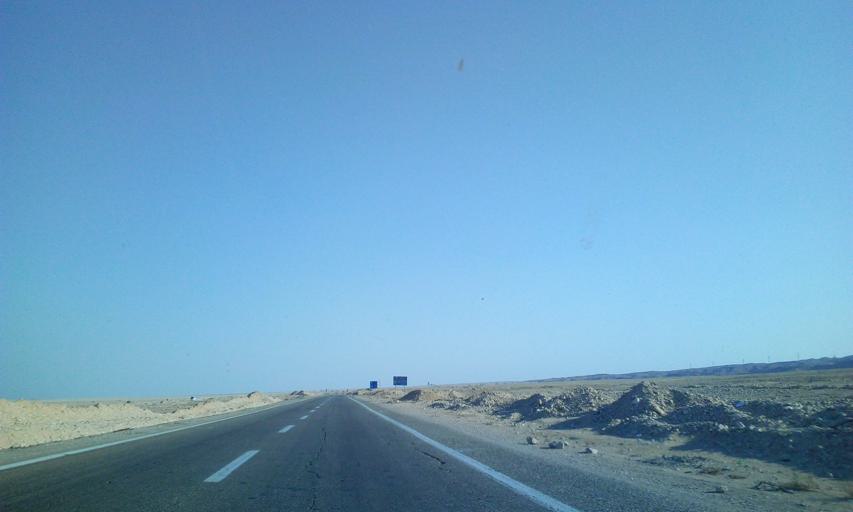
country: EG
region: As Suways
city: Ain Sukhna
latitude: 28.9623
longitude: 32.6199
